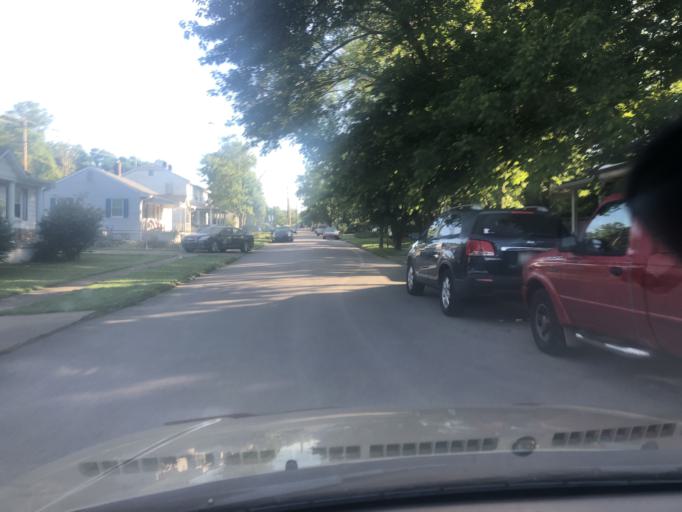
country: US
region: Tennessee
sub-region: Davidson County
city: Lakewood
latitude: 36.2561
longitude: -86.6509
